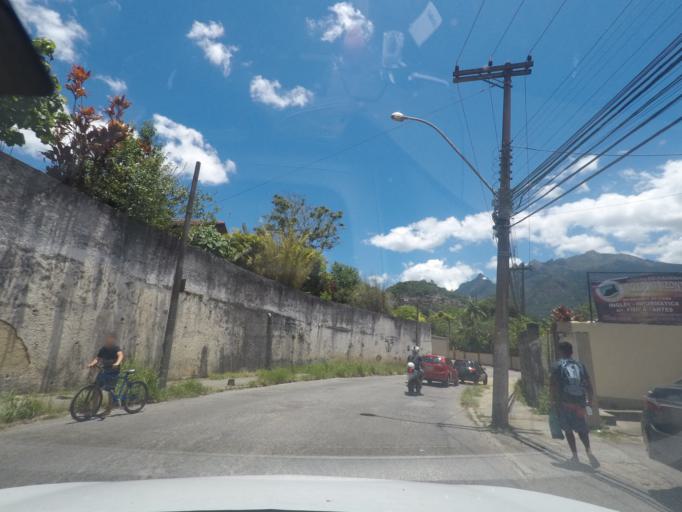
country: BR
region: Rio de Janeiro
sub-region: Teresopolis
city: Teresopolis
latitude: -22.4343
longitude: -42.9675
